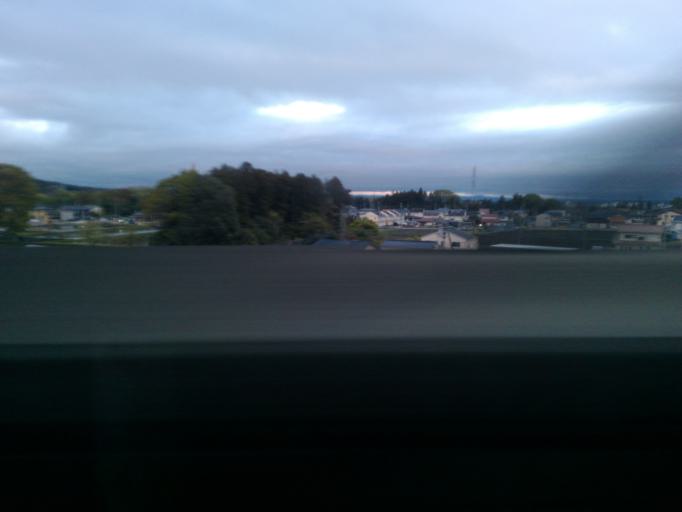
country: JP
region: Tochigi
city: Otawara
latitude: 36.8920
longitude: 139.9919
